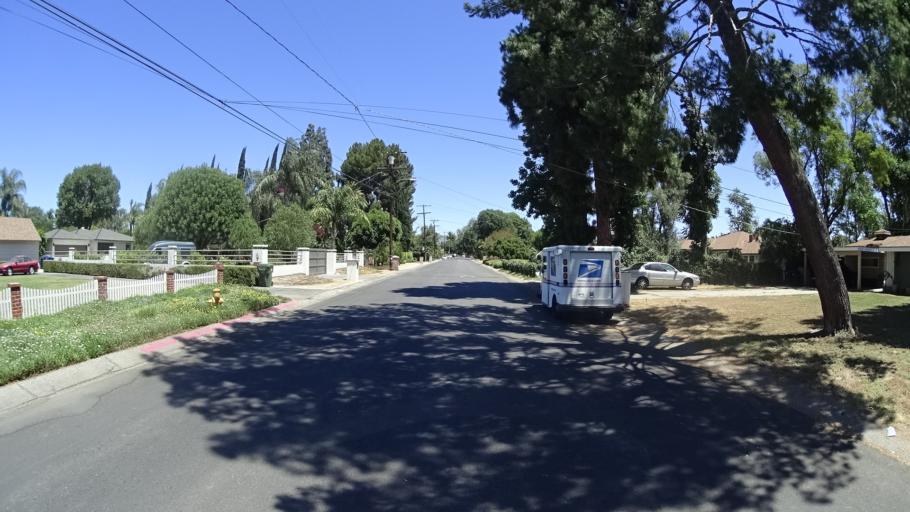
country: US
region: California
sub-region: Los Angeles County
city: San Fernando
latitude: 34.2444
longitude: -118.4698
